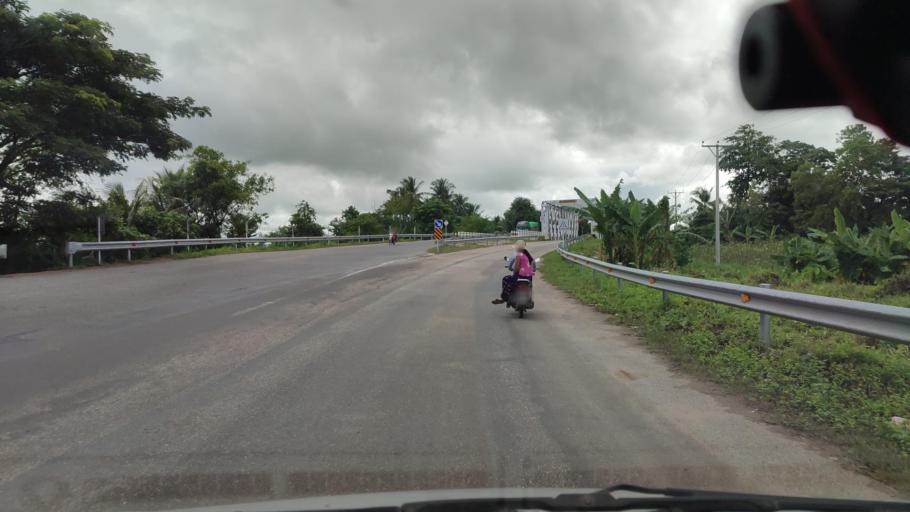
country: MM
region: Bago
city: Letpandan
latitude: 18.1599
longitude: 95.6913
